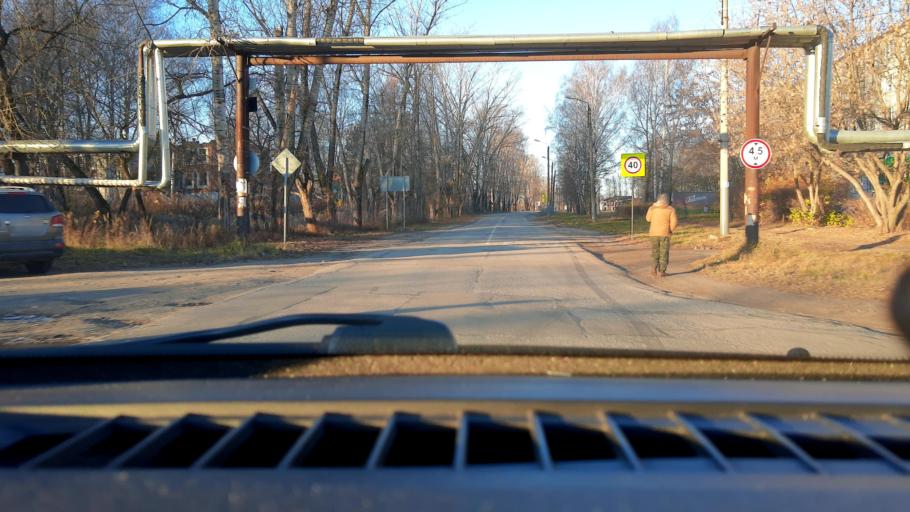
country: RU
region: Nizjnij Novgorod
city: Kstovo
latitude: 56.1811
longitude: 44.1658
